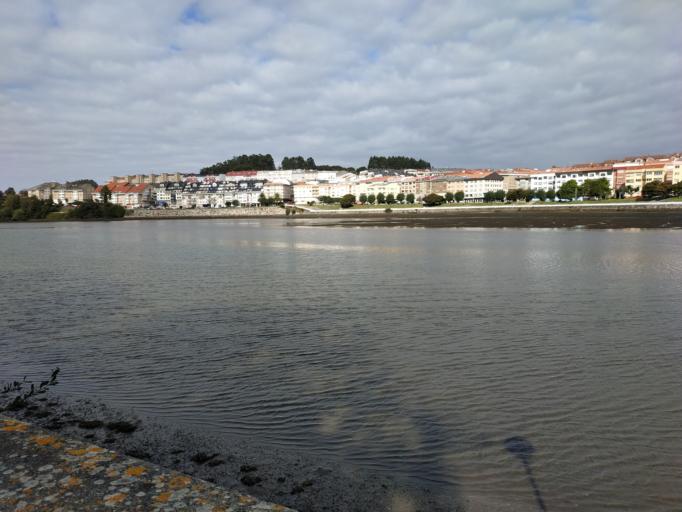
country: ES
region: Galicia
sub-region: Provincia da Coruna
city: Cambre
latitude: 43.3170
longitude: -8.3610
